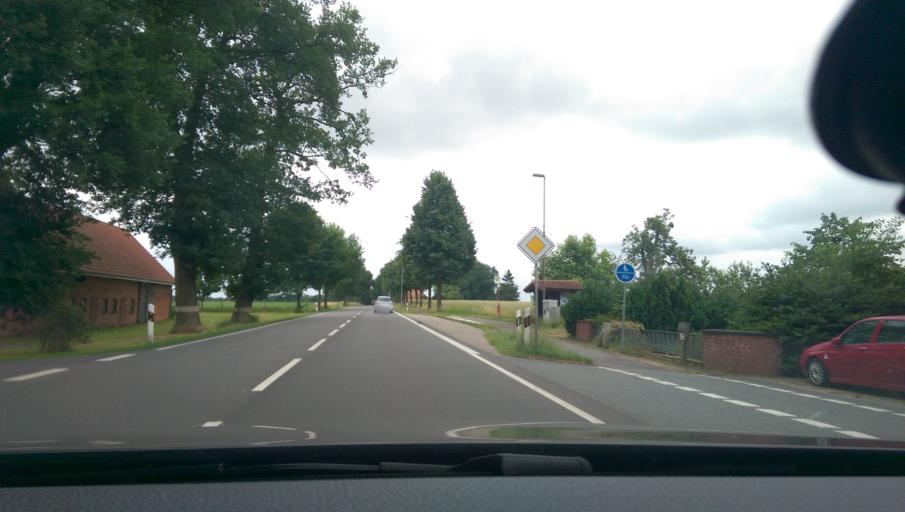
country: DE
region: Lower Saxony
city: Gyhum
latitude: 53.1750
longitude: 9.2928
